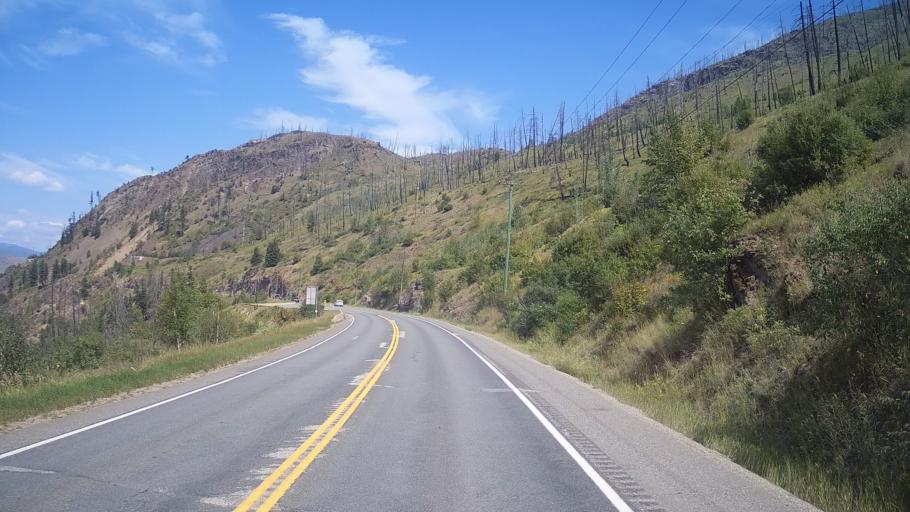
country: CA
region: British Columbia
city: Kamloops
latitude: 51.1000
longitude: -120.1428
